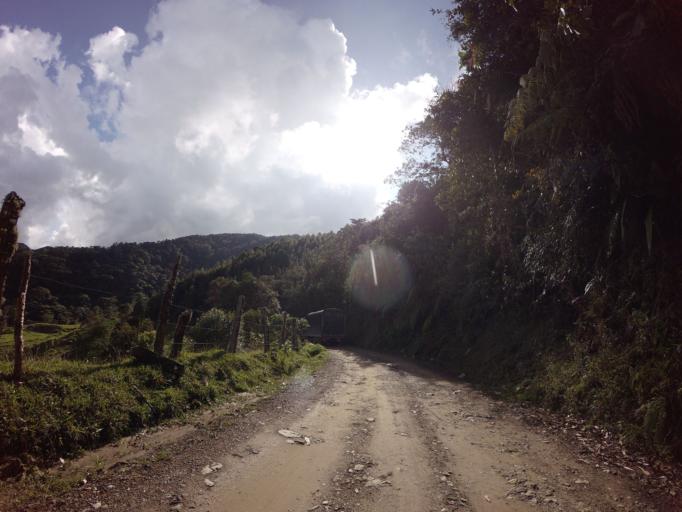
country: CO
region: Caldas
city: Pensilvania
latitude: 5.4572
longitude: -75.1237
